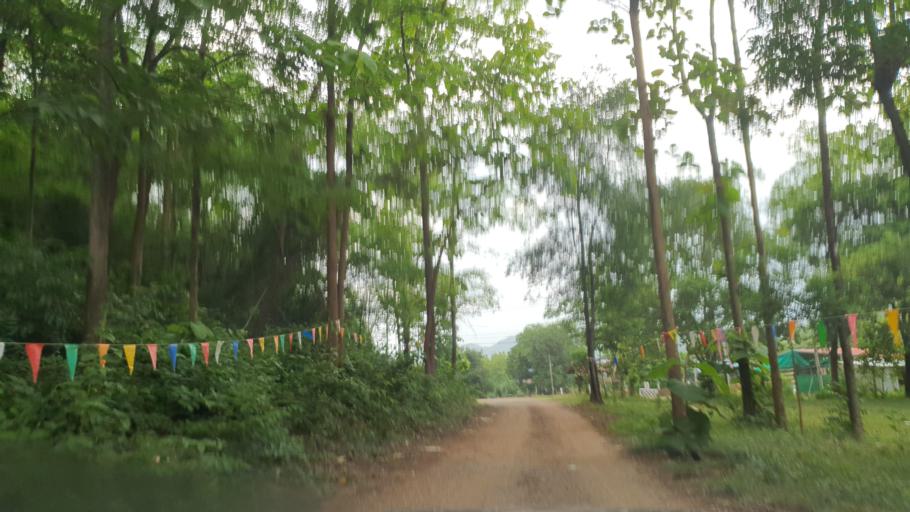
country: TH
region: Sukhothai
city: Thung Saliam
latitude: 17.2643
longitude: 99.5357
